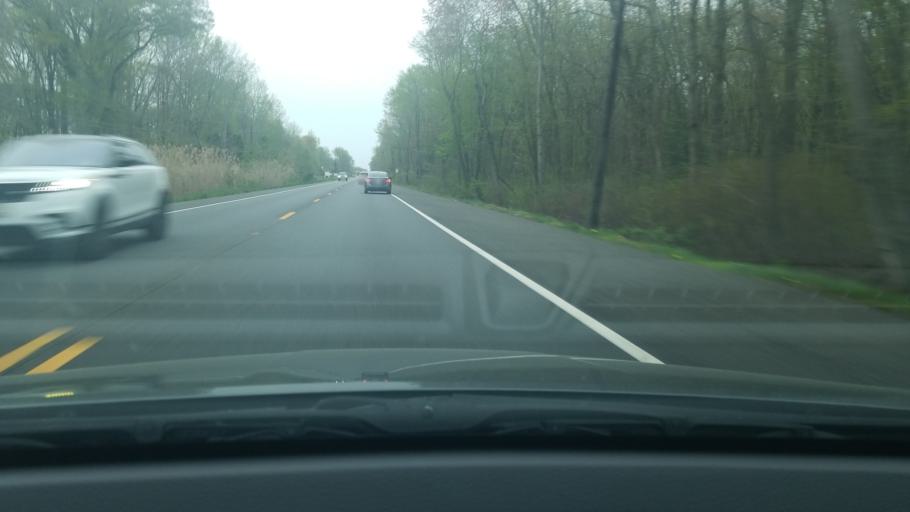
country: US
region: New Jersey
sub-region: Burlington County
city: Mount Laurel
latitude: 39.8965
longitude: -74.8677
